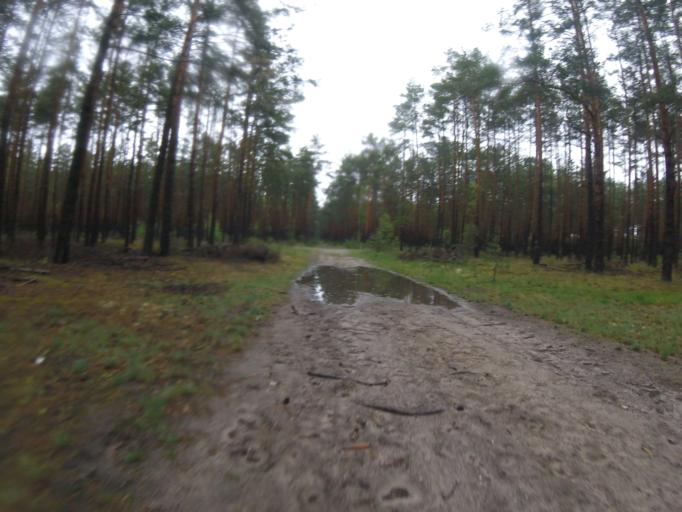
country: DE
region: Brandenburg
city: Schwerin
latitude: 52.1356
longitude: 13.6356
